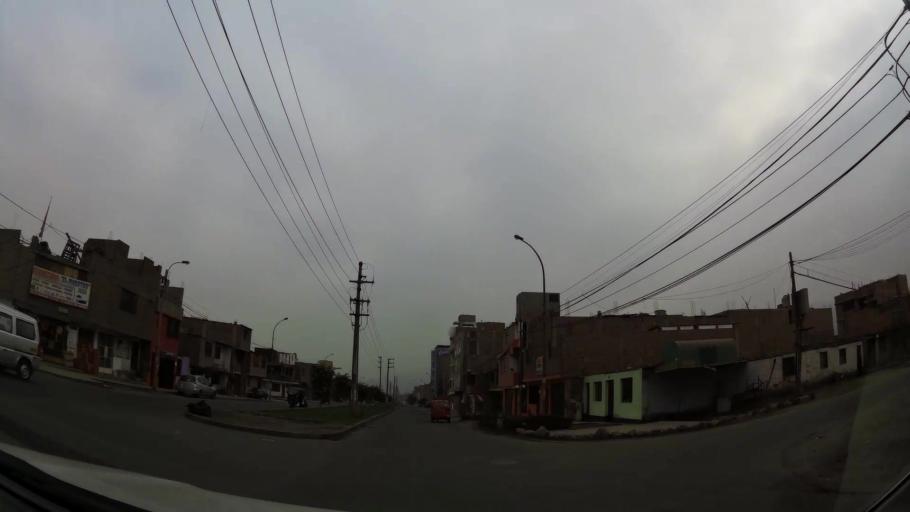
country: PE
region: Lima
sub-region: Lima
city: Independencia
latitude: -11.9651
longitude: -76.9955
